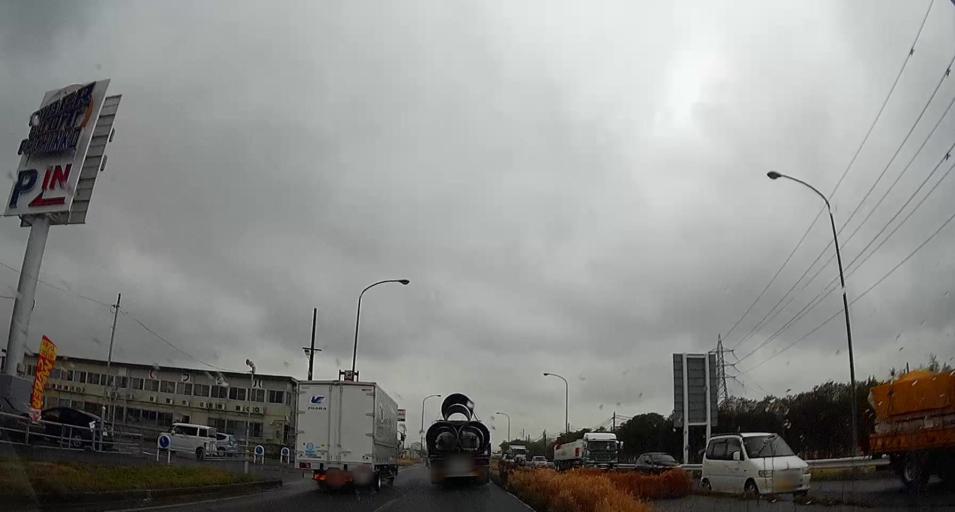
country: JP
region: Chiba
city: Ichihara
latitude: 35.5314
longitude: 140.1039
